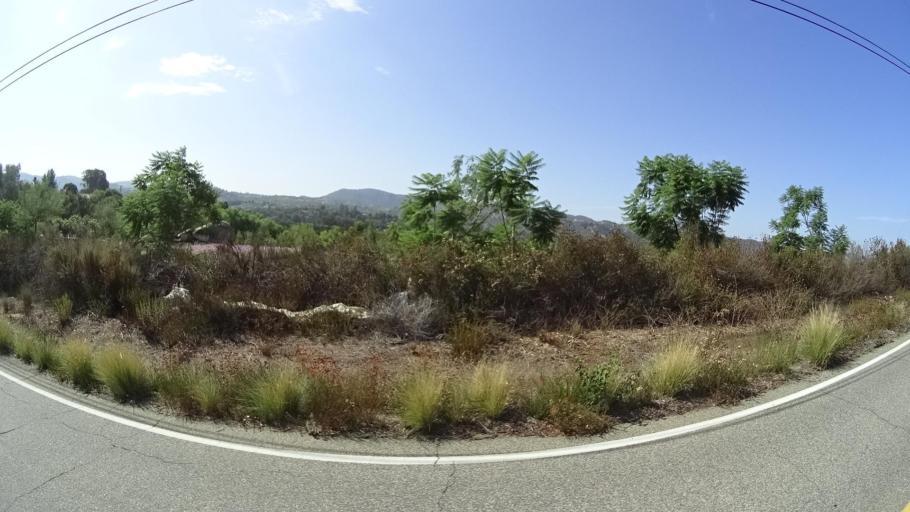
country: US
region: California
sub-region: San Diego County
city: Valley Center
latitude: 33.2356
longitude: -116.9897
